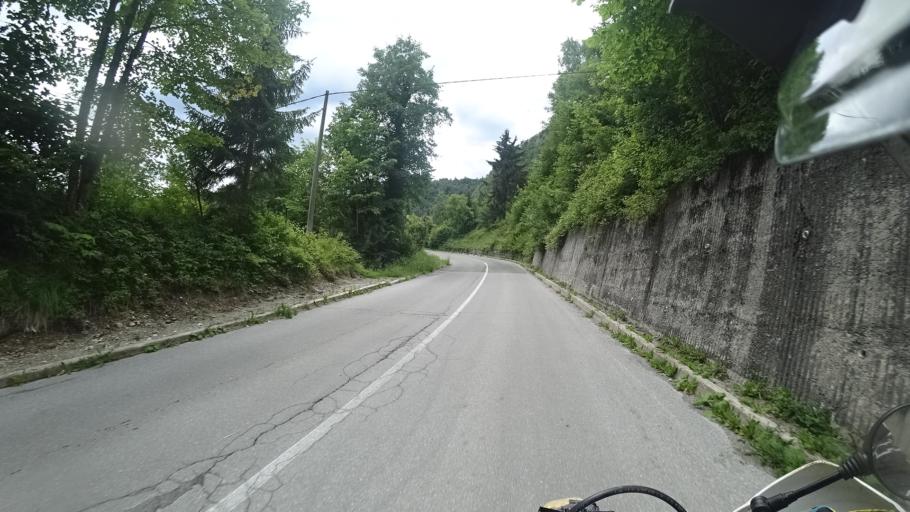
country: SI
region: Osilnica
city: Osilnica
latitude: 45.5984
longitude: 14.6392
